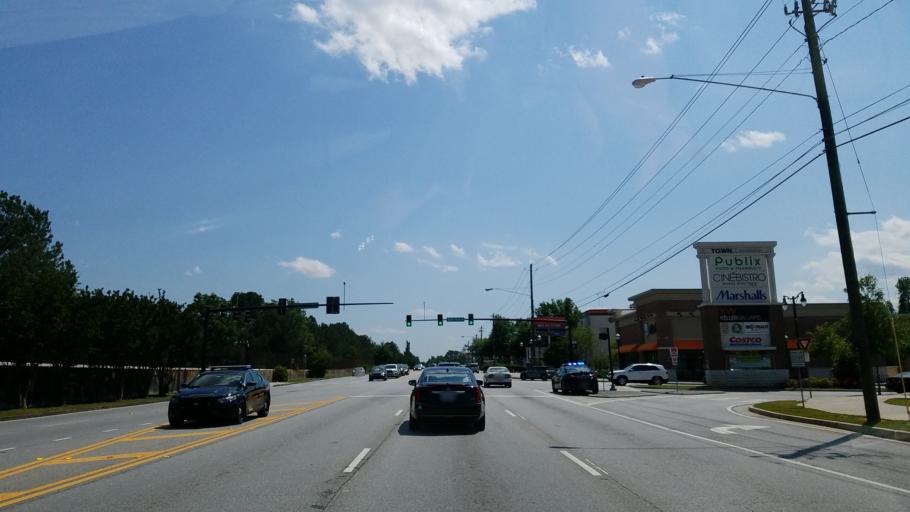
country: US
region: Georgia
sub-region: DeKalb County
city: North Atlanta
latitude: 33.8697
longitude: -84.3340
